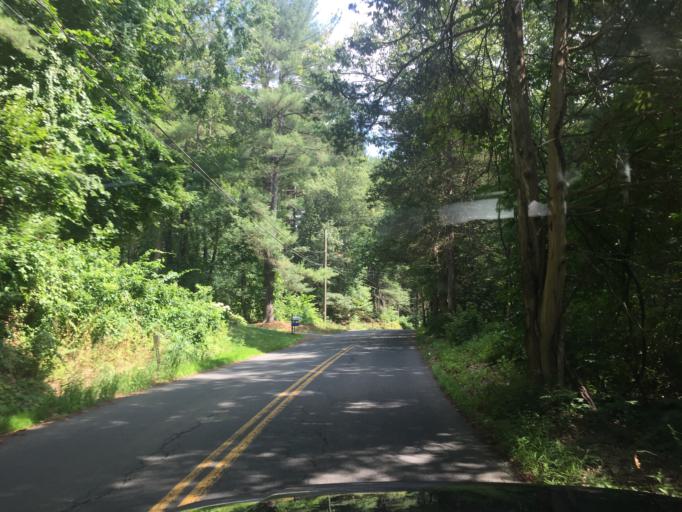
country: US
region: Connecticut
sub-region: Hartford County
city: Salmon Brook
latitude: 41.9571
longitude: -72.7803
